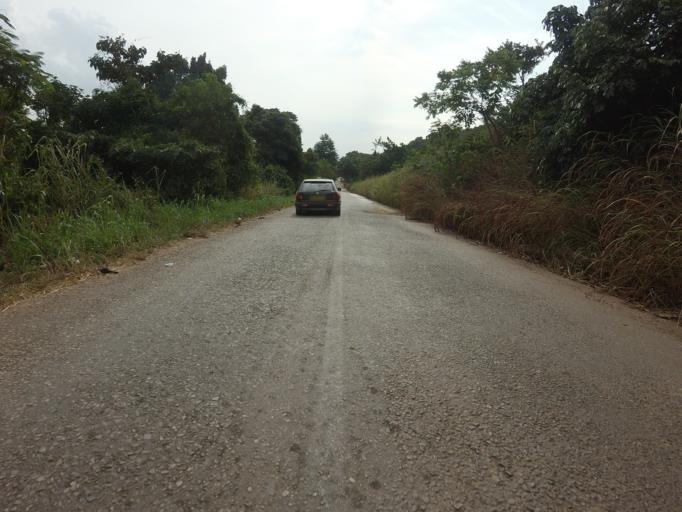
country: GH
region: Volta
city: Ho
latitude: 6.6830
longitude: 0.3393
